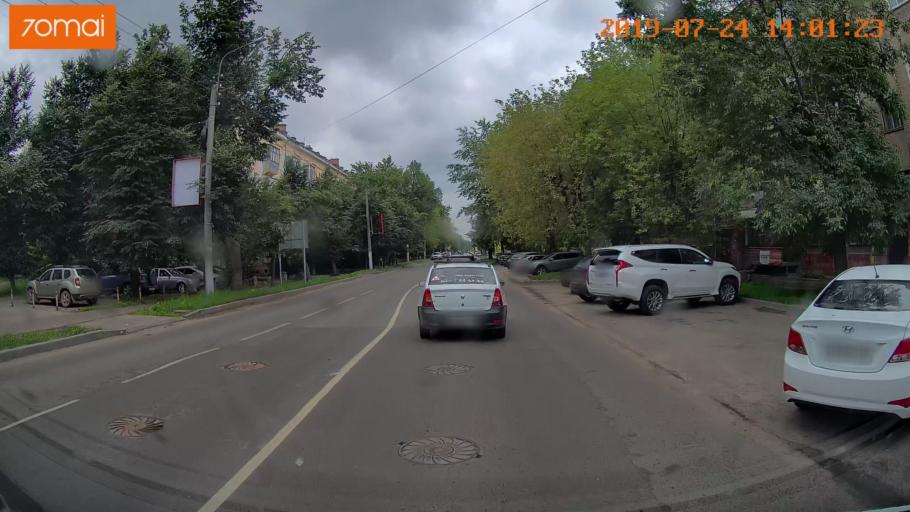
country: RU
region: Ivanovo
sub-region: Gorod Ivanovo
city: Ivanovo
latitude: 57.0103
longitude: 40.9794
